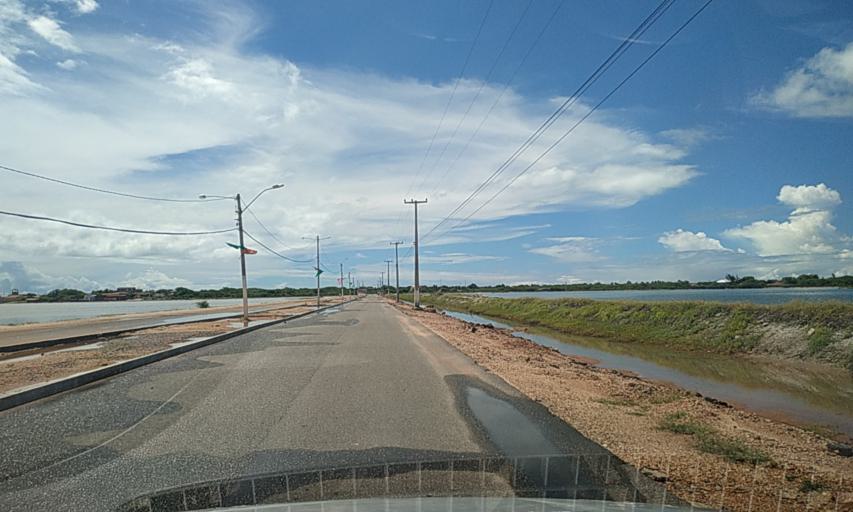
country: BR
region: Rio Grande do Norte
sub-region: Areia Branca
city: Areia Branca
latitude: -4.9394
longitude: -37.1129
